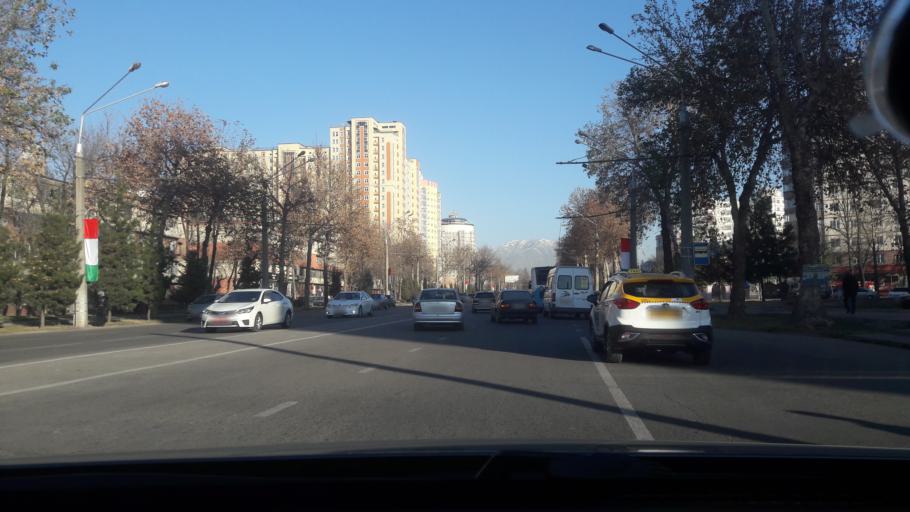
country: TJ
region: Dushanbe
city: Dushanbe
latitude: 38.5592
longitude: 68.7551
